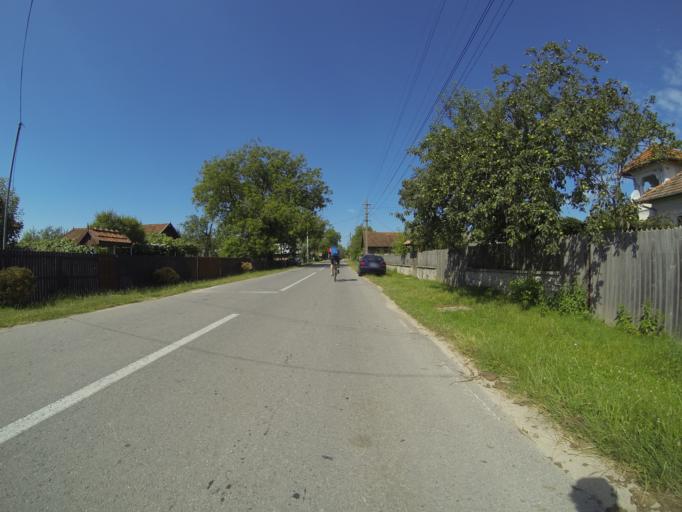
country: RO
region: Gorj
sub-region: Comuna Polovragi
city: Polovragi
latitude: 45.1673
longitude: 23.8161
